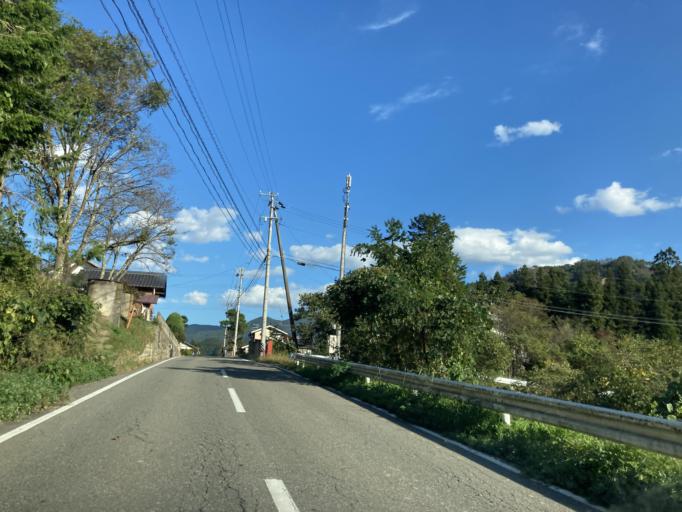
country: JP
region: Nagano
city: Omachi
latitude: 36.4397
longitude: 137.9946
